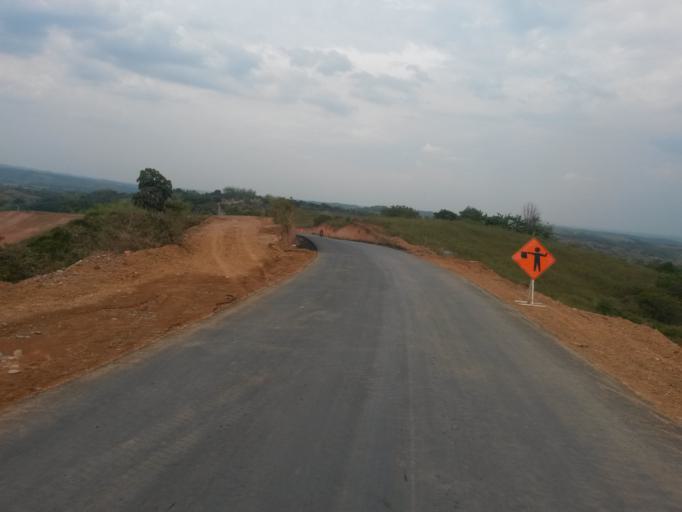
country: CO
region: Cauca
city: Buenos Aires
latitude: 3.0631
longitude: -76.6226
